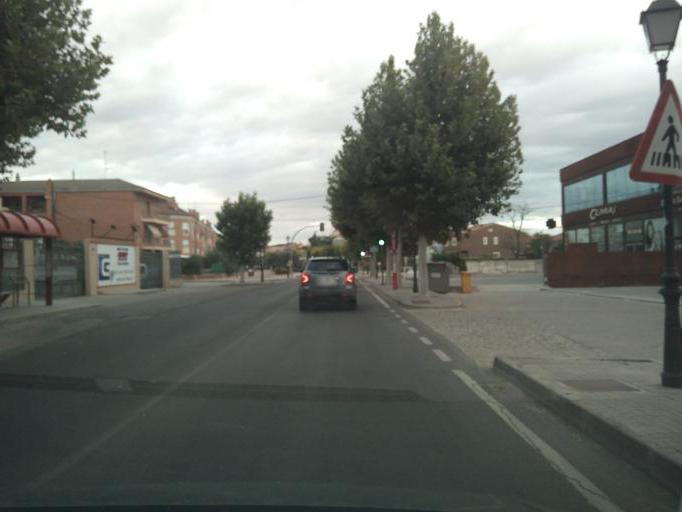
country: ES
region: Madrid
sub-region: Provincia de Madrid
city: Ajalvir
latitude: 40.5312
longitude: -3.4808
